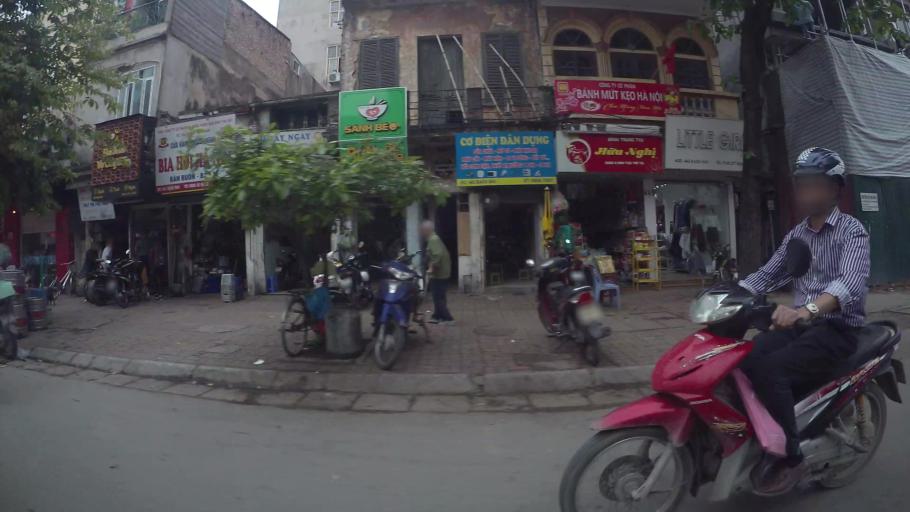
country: VN
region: Ha Noi
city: Hai BaTrung
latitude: 20.9981
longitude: 105.8502
